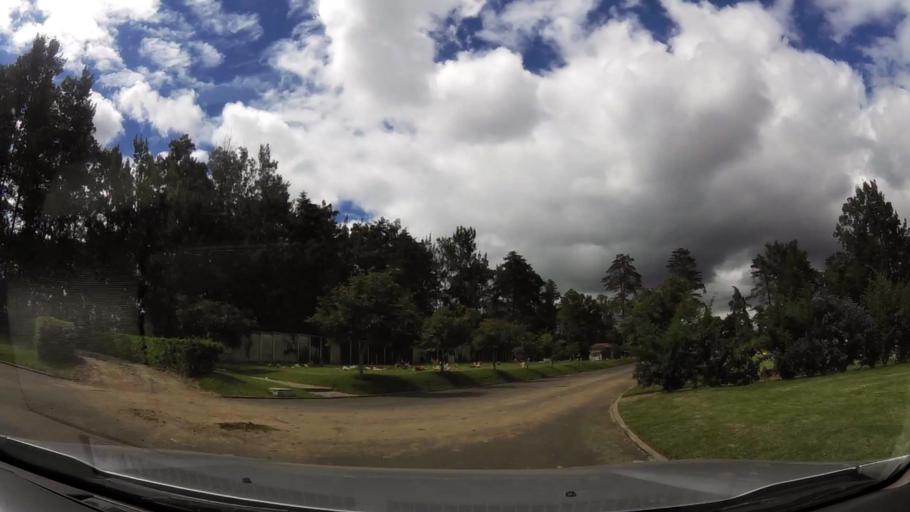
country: GT
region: Guatemala
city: Chinautla
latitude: 14.6868
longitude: -90.5410
